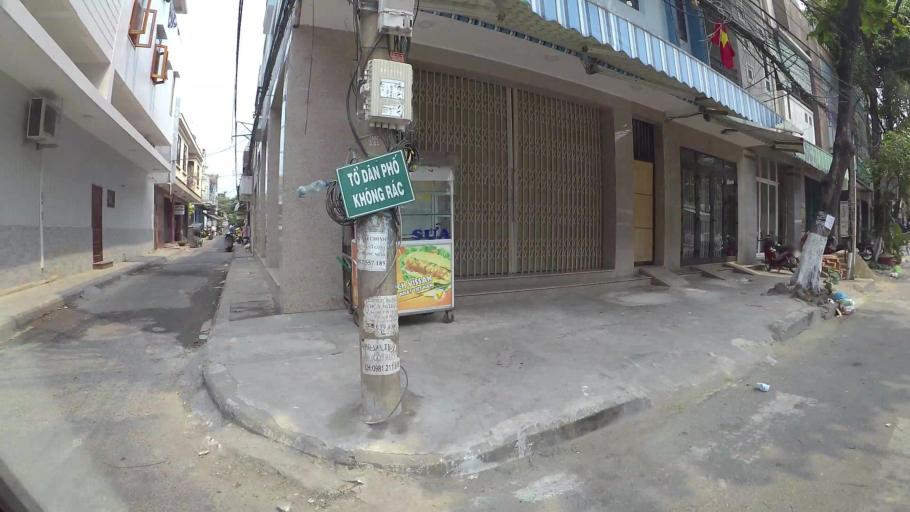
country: VN
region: Da Nang
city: Da Nang
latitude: 16.0497
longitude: 108.2166
